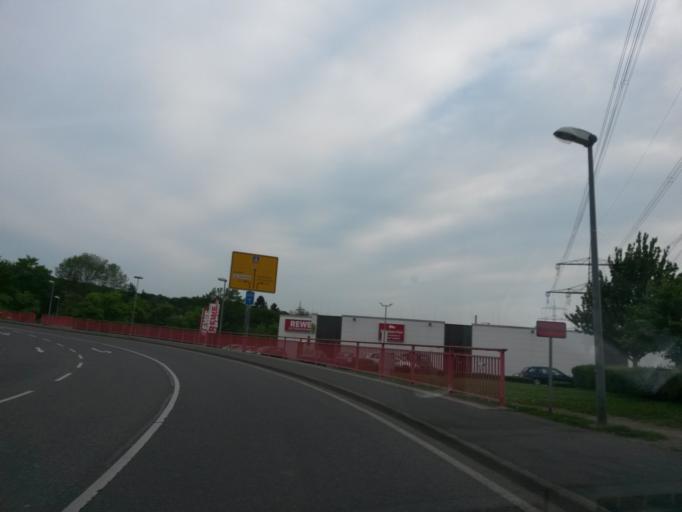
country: DE
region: North Rhine-Westphalia
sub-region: Regierungsbezirk Koln
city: Alfter
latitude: 50.7156
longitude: 7.0264
